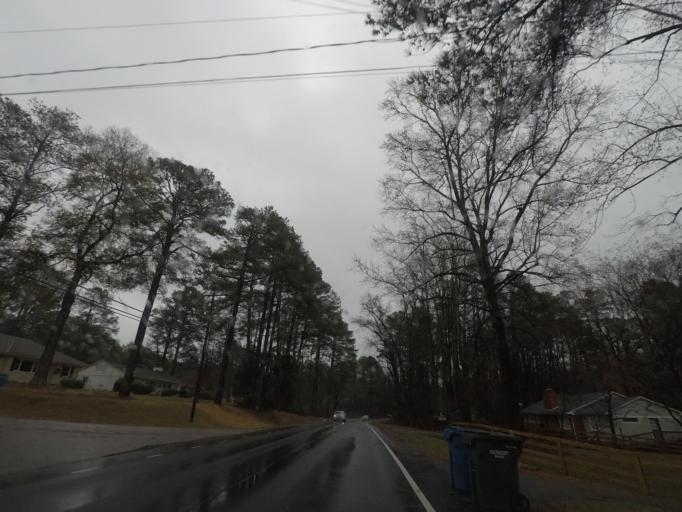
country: US
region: North Carolina
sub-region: Durham County
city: Durham
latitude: 36.0449
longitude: -78.9670
